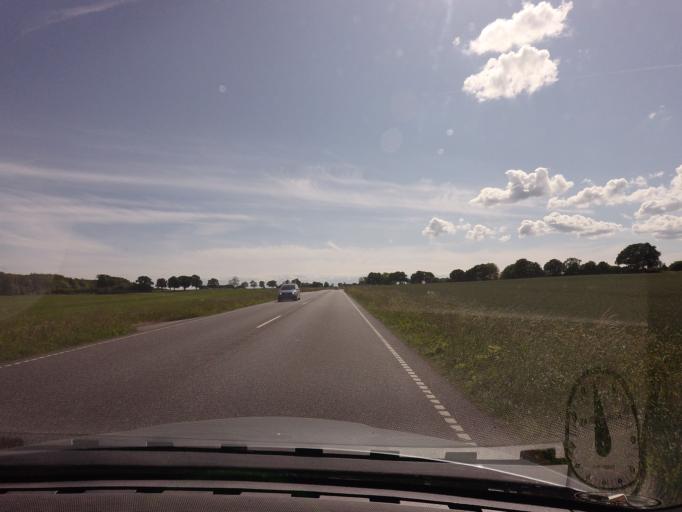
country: DK
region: Central Jutland
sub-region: Syddjurs Kommune
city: Ebeltoft
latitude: 56.3167
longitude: 10.7063
